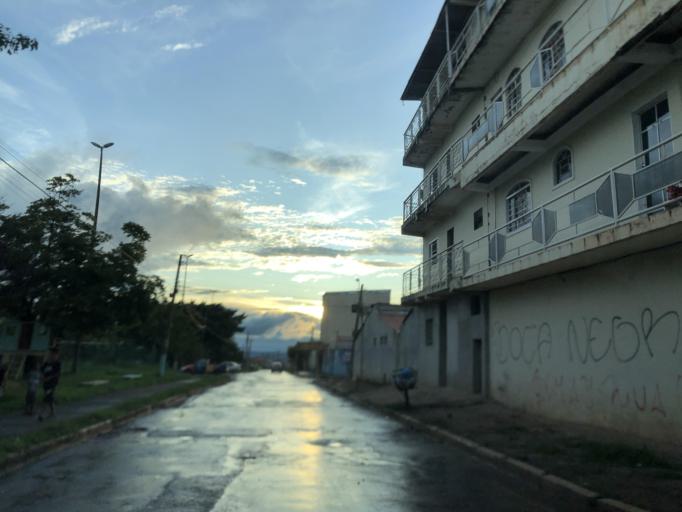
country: BR
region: Federal District
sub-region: Brasilia
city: Brasilia
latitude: -15.8322
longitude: -48.1031
